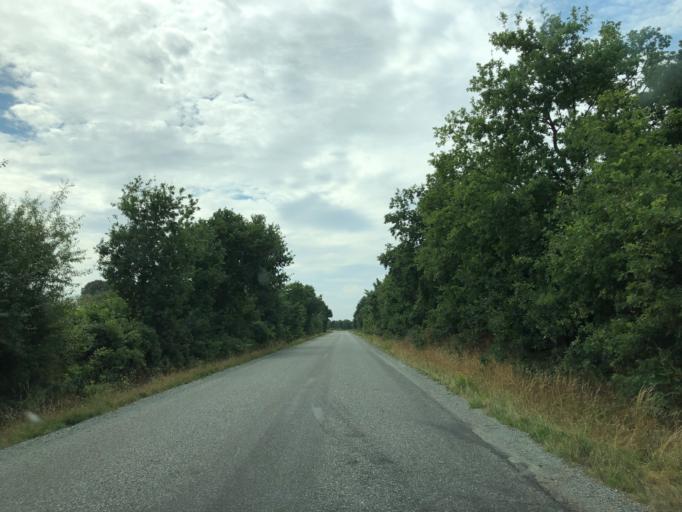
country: DK
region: South Denmark
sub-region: Vejle Kommune
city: Egtved
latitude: 55.6122
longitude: 9.1886
